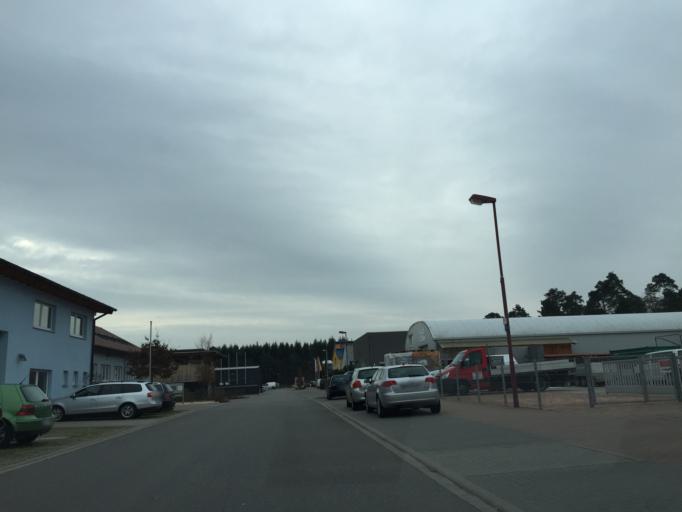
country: DE
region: Baden-Wuerttemberg
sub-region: Karlsruhe Region
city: Oftersheim
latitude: 49.3551
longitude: 8.5850
